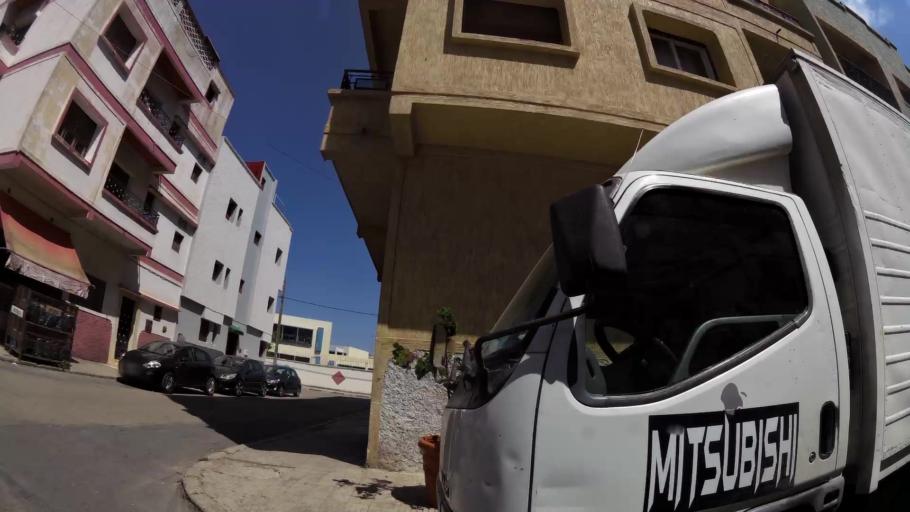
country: MA
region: Rabat-Sale-Zemmour-Zaer
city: Sale
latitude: 34.0451
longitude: -6.7882
